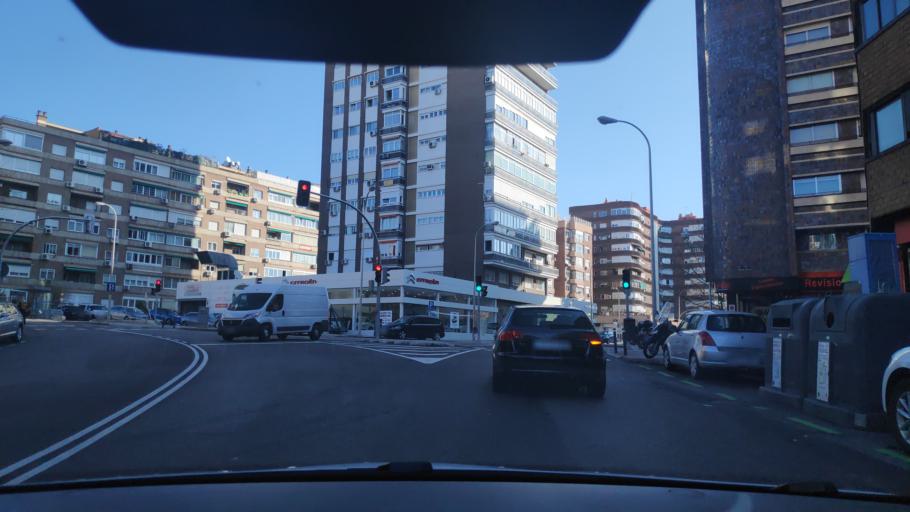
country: ES
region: Madrid
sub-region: Provincia de Madrid
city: Chamartin
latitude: 40.4562
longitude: -3.6811
